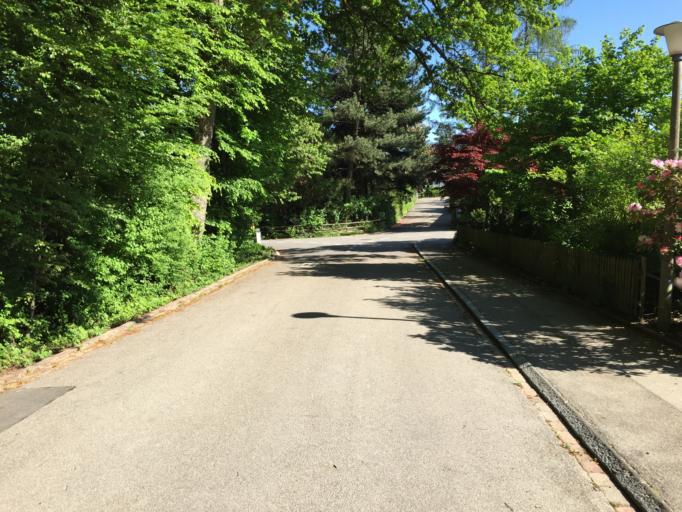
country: CH
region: Zurich
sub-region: Bezirk Uster
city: Pfaffhausen
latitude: 47.3671
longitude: 8.6230
